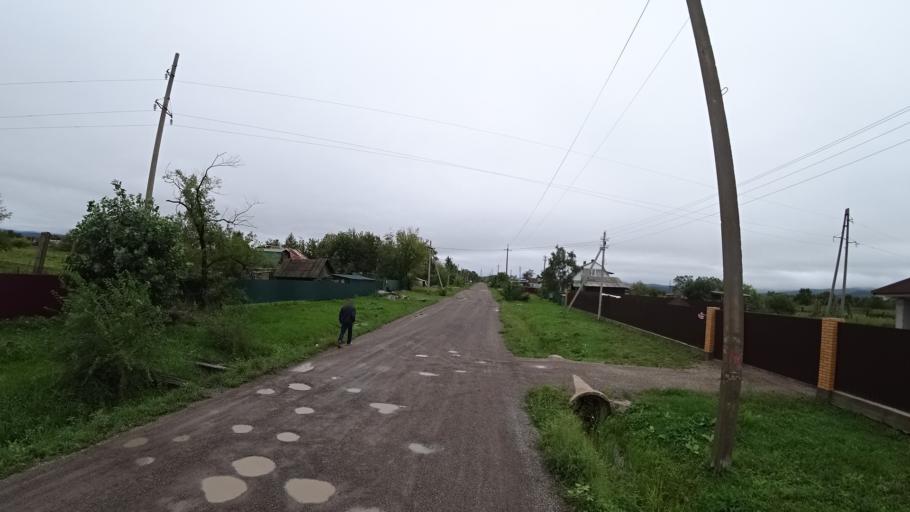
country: RU
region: Primorskiy
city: Monastyrishche
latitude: 44.1984
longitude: 132.4557
